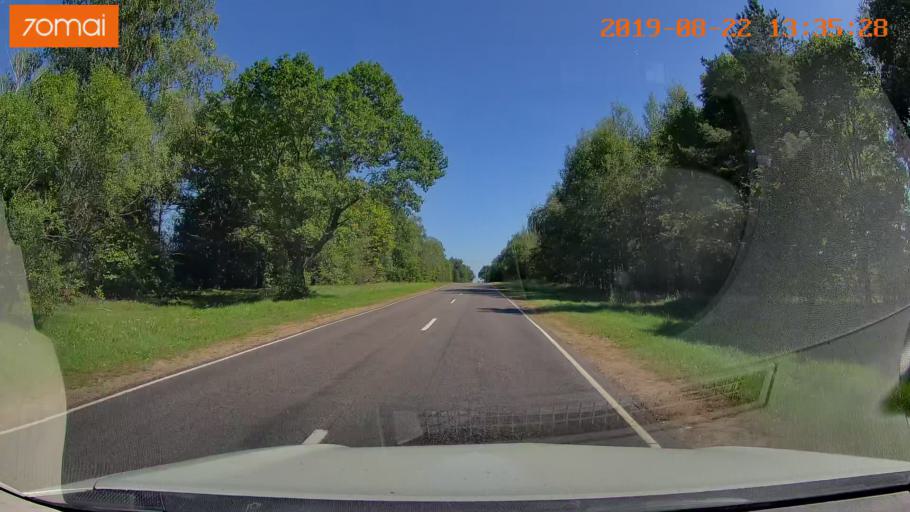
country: BY
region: Minsk
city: Staryya Darohi
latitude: 53.2136
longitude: 28.2690
